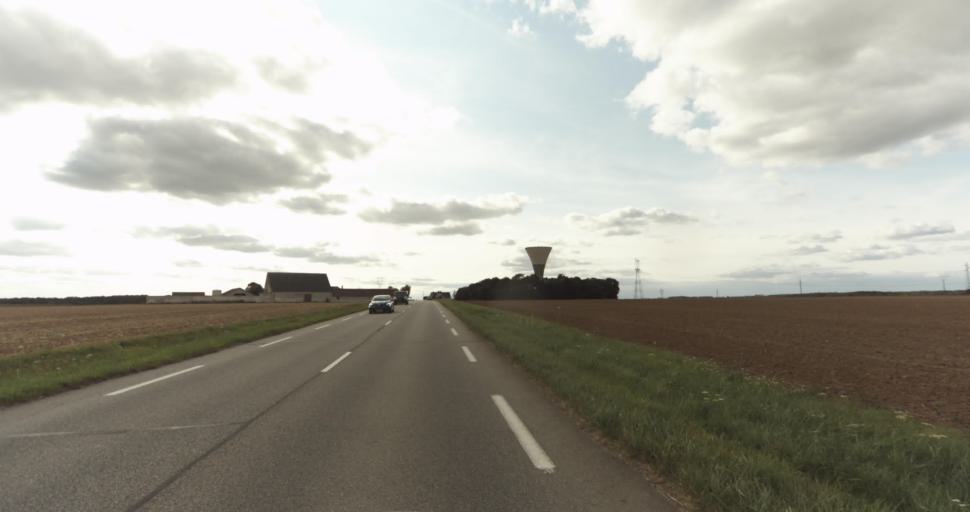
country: FR
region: Haute-Normandie
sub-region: Departement de l'Eure
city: Garennes-sur-Eure
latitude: 48.8910
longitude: 1.4342
